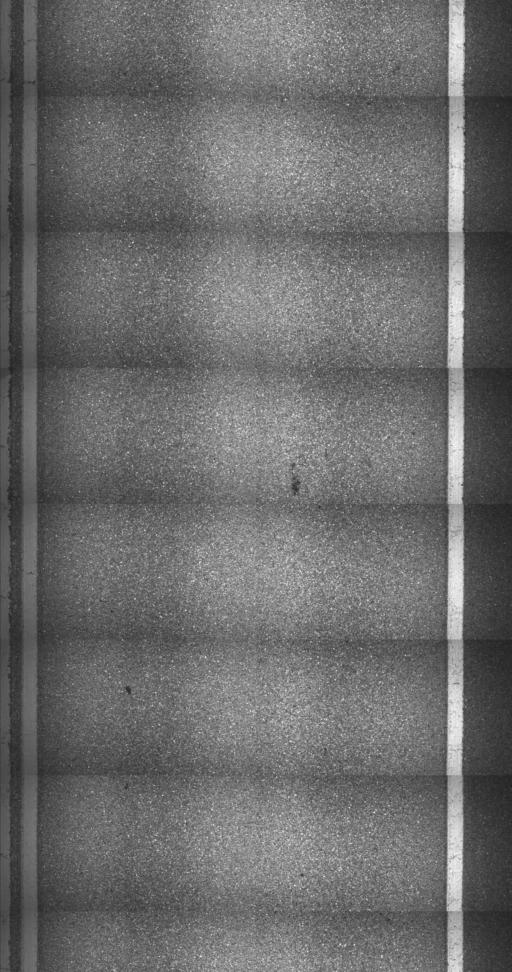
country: US
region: Vermont
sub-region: Bennington County
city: Arlington
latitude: 43.1190
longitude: -73.1064
